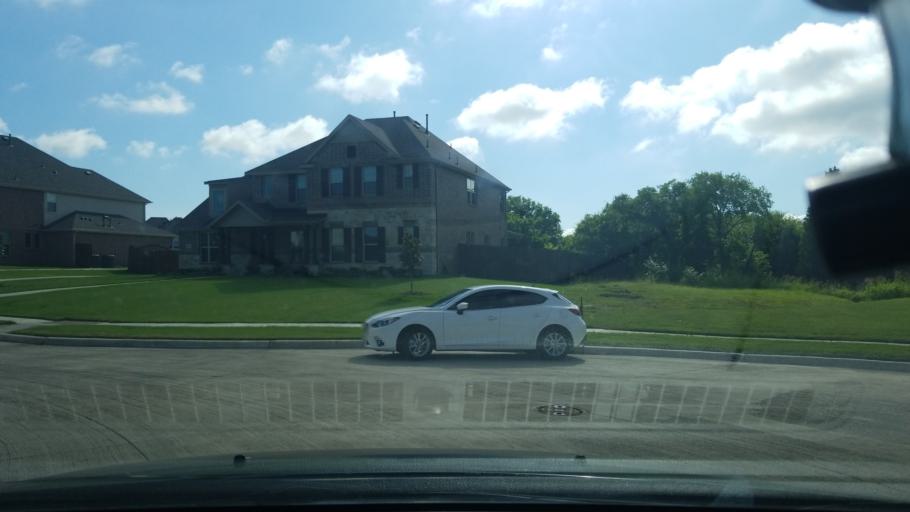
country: US
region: Texas
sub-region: Dallas County
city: Sunnyvale
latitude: 32.8008
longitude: -96.5675
